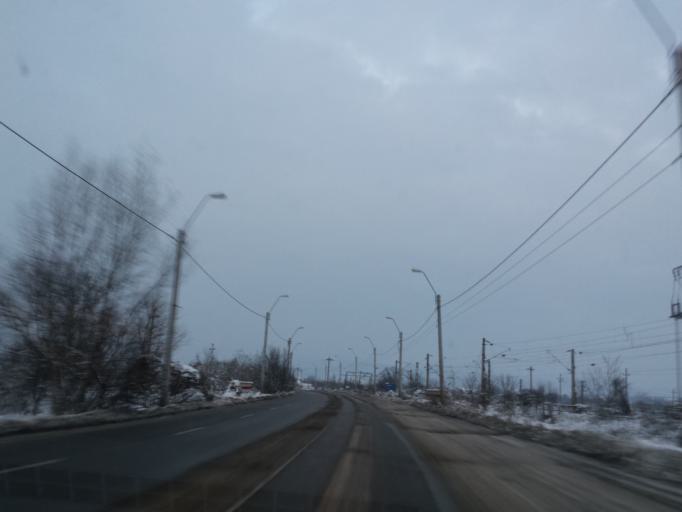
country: RO
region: Hunedoara
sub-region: Municipiul Deva
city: Cristur
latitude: 45.8244
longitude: 22.9437
